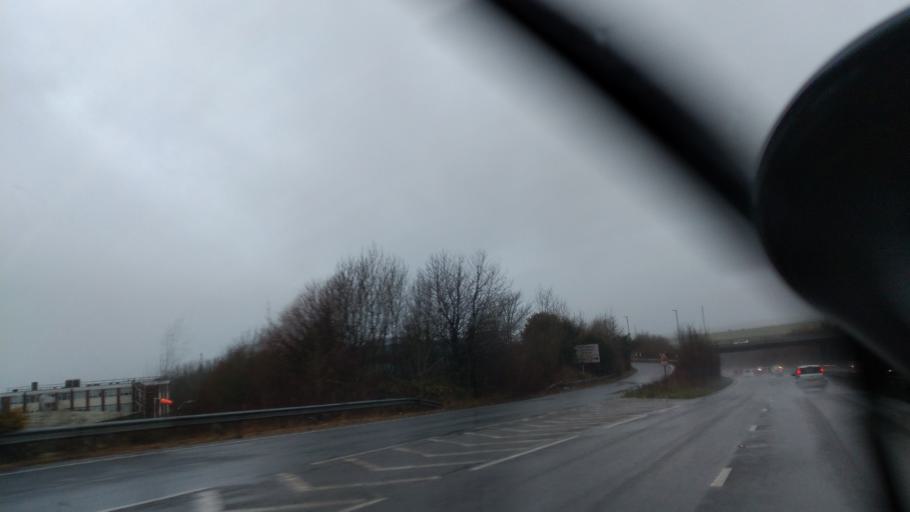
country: GB
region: England
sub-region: Brighton and Hove
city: Brighton
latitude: 50.8697
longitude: -0.1206
